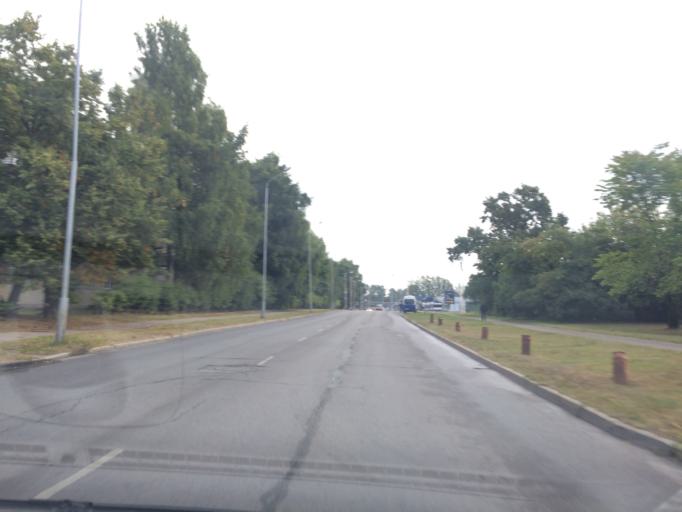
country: LV
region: Kekava
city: Kekava
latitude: 56.8984
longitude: 24.2135
